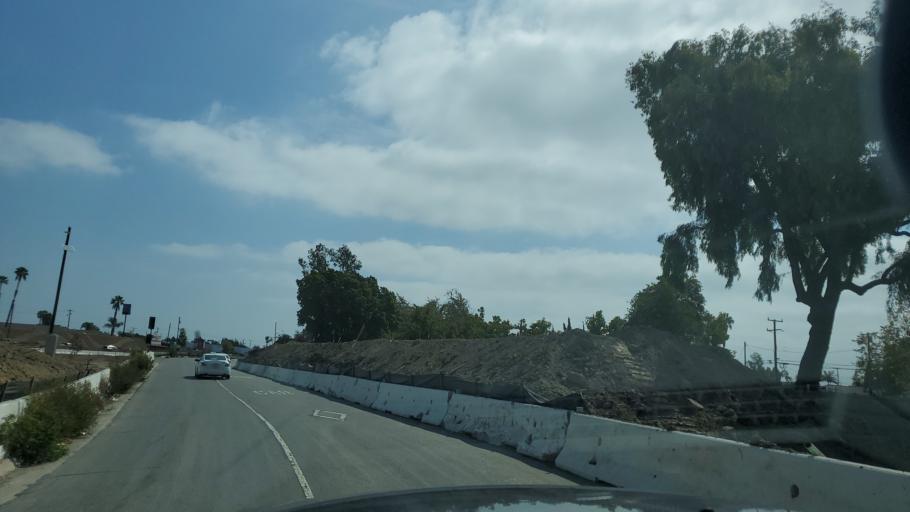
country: US
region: California
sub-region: Orange County
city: Westminster
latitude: 33.7579
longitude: -118.0227
